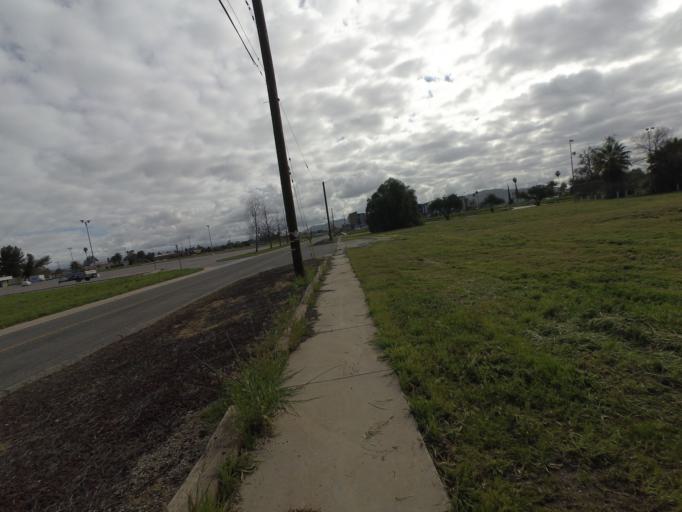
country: US
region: California
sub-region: Riverside County
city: March Air Force Base
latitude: 33.8990
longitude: -117.2508
